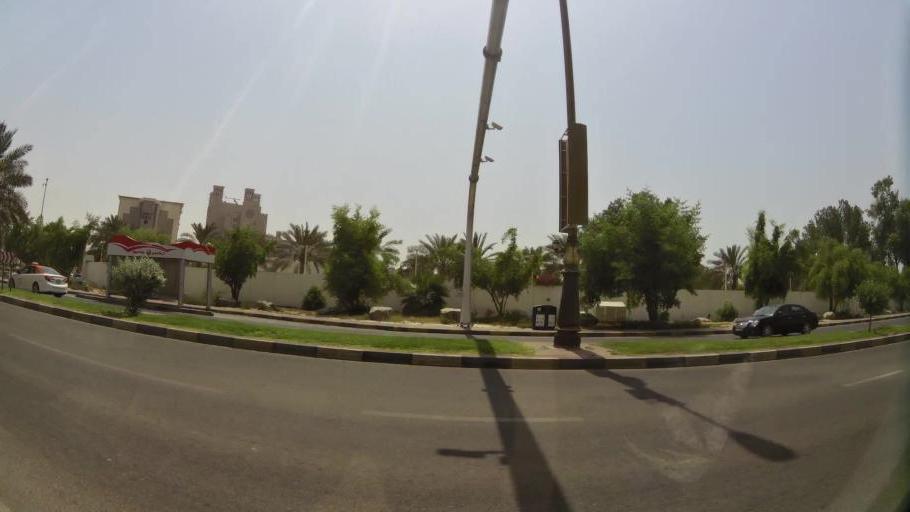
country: AE
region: Ajman
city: Ajman
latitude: 25.3974
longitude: 55.4253
